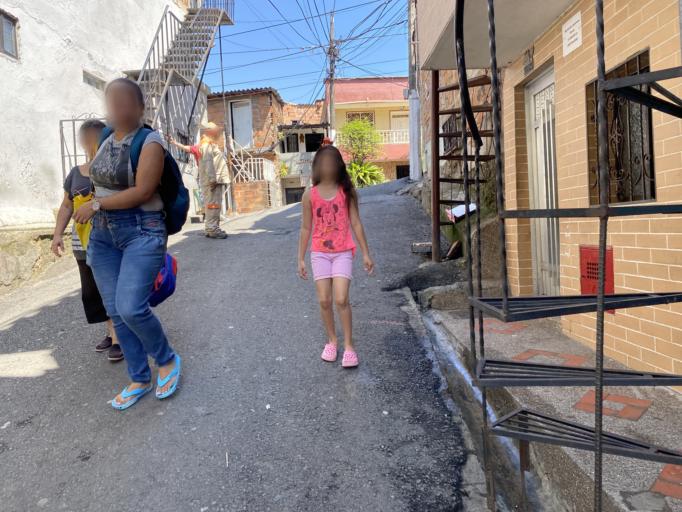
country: CO
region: Antioquia
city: Bello
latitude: 6.3012
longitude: -75.5459
